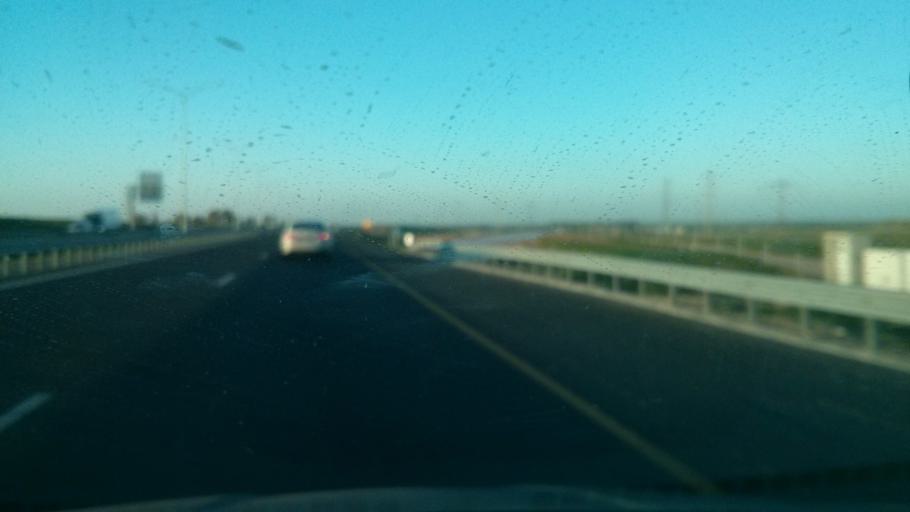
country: IL
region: Southern District
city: Lehavim
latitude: 31.4535
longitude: 34.7703
